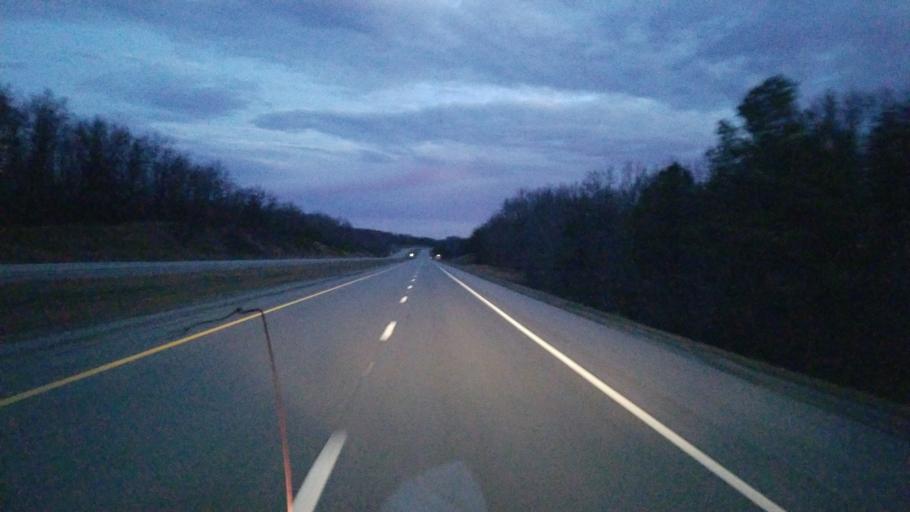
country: US
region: Tennessee
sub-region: Van Buren County
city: Spencer
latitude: 35.5704
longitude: -85.4715
